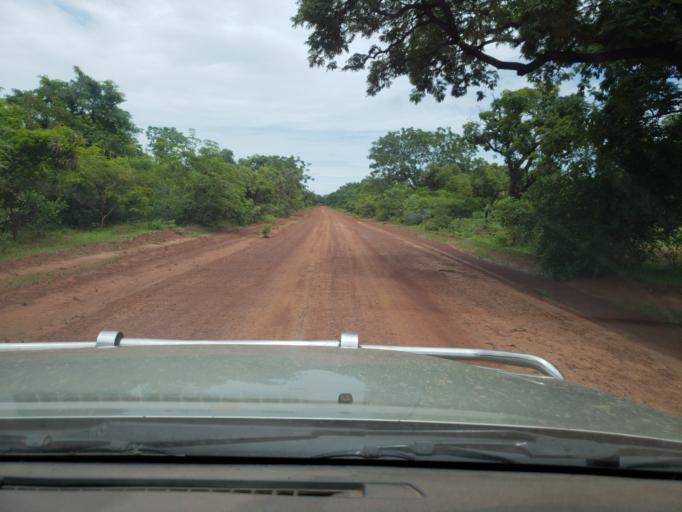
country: ML
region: Sikasso
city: Sikasso
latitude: 11.6632
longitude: -6.3421
